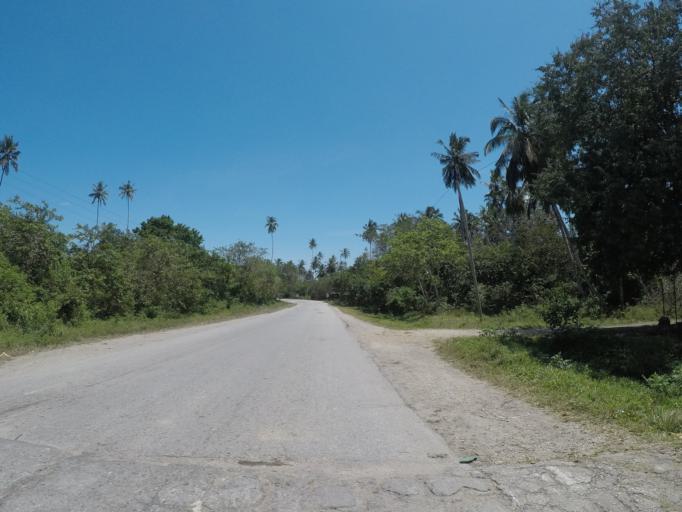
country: TZ
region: Zanzibar Central/South
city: Nganane
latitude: -6.2721
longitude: 39.4203
